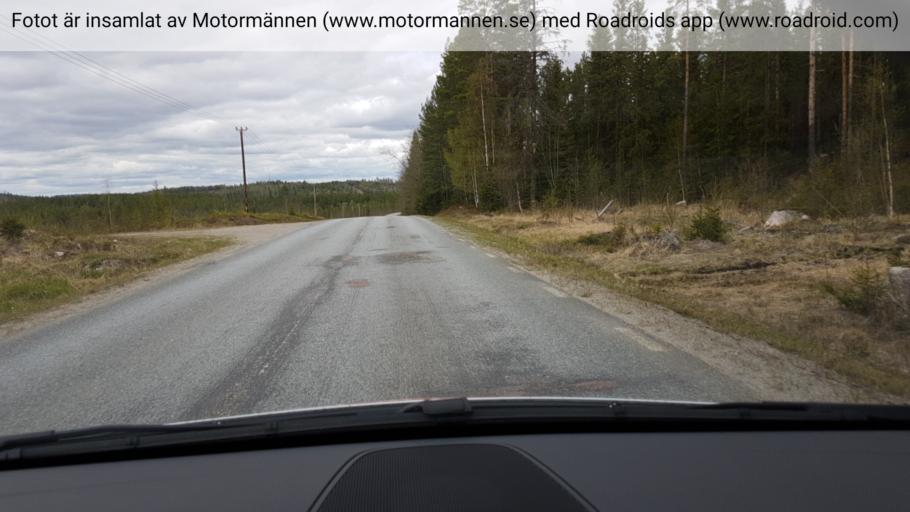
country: SE
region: Jaemtland
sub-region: Braecke Kommun
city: Braecke
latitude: 62.8249
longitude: 15.4607
